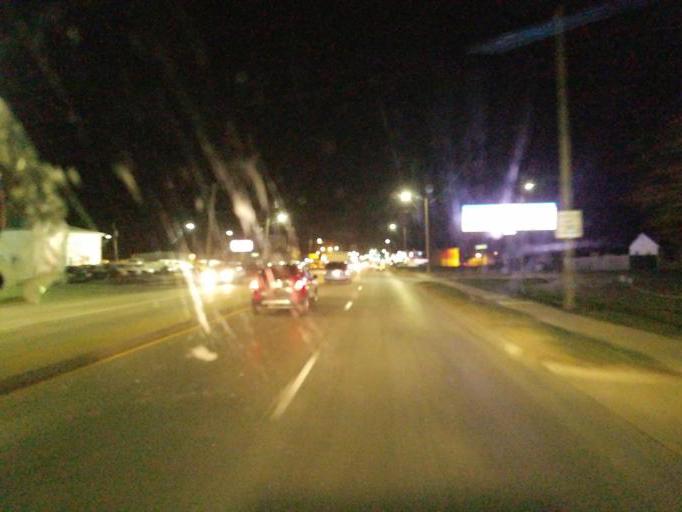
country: US
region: Iowa
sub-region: Polk County
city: Des Moines
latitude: 41.6005
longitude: -93.5650
